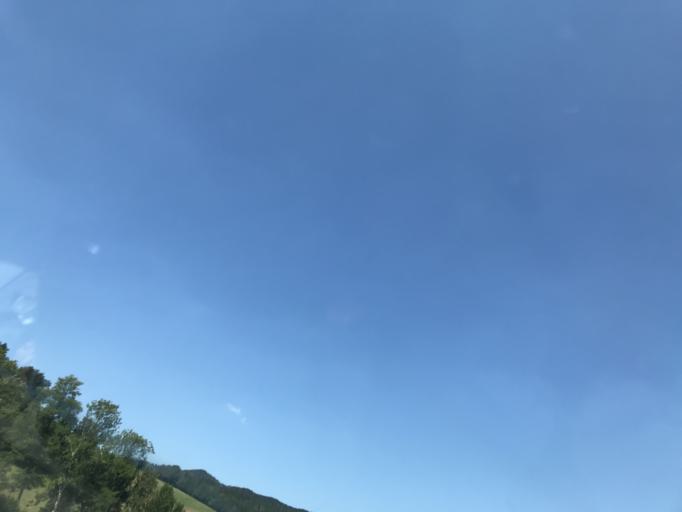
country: DE
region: Baden-Wuerttemberg
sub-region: Freiburg Region
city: Stegen
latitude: 47.9870
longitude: 7.9725
